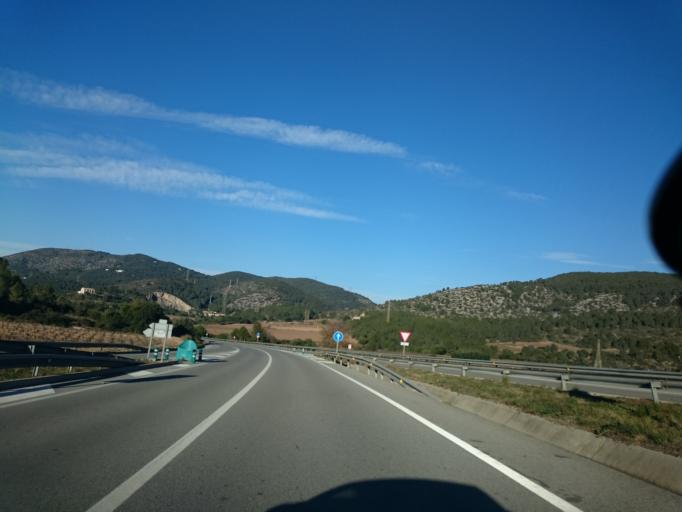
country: ES
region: Catalonia
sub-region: Provincia de Barcelona
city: Sant Pere de Ribes
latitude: 41.2654
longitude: 1.7790
